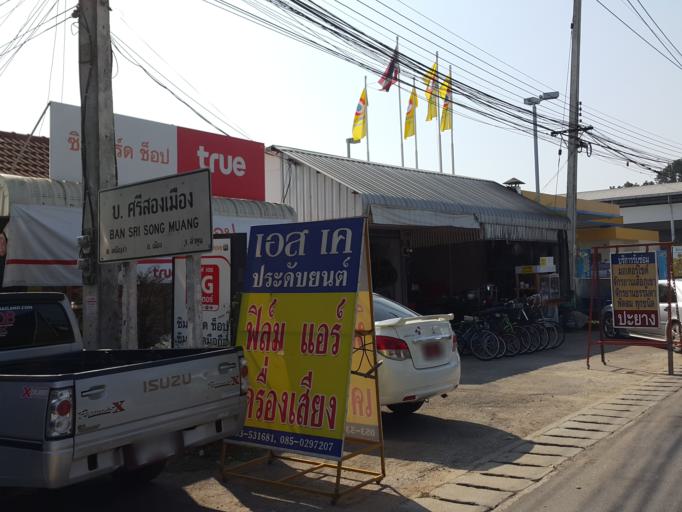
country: TH
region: Lamphun
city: Lamphun
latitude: 18.6046
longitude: 99.0232
